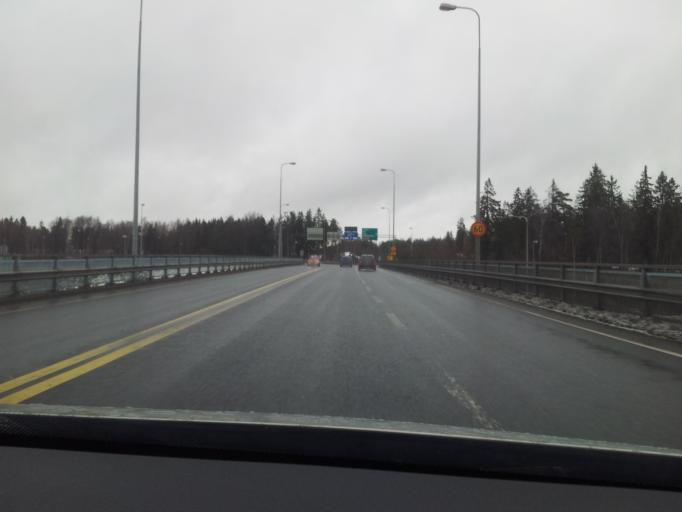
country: FI
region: Uusimaa
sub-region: Helsinki
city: Kauniainen
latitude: 60.2042
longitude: 24.7465
